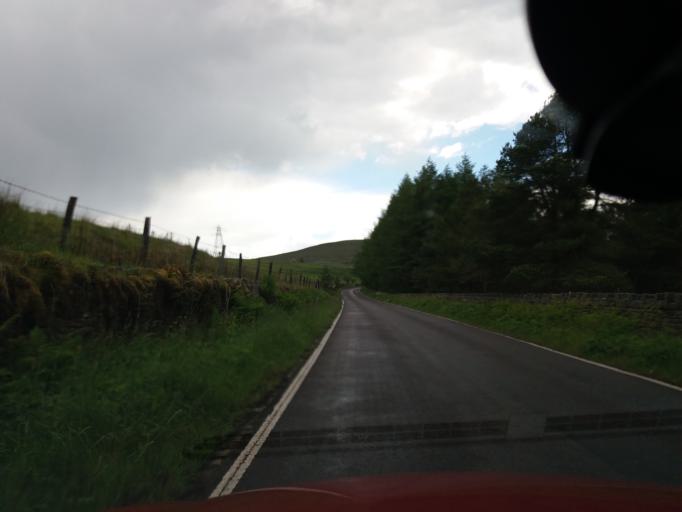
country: GB
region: England
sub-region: Blackburn with Darwen
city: Darwen
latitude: 53.6530
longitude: -2.4462
